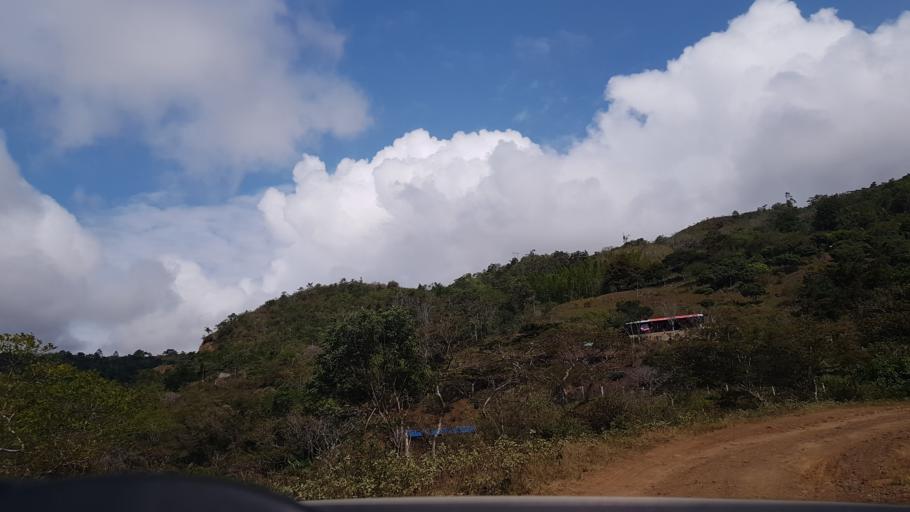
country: CO
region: Valle del Cauca
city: Yumbo
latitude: 3.6528
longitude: -76.5154
